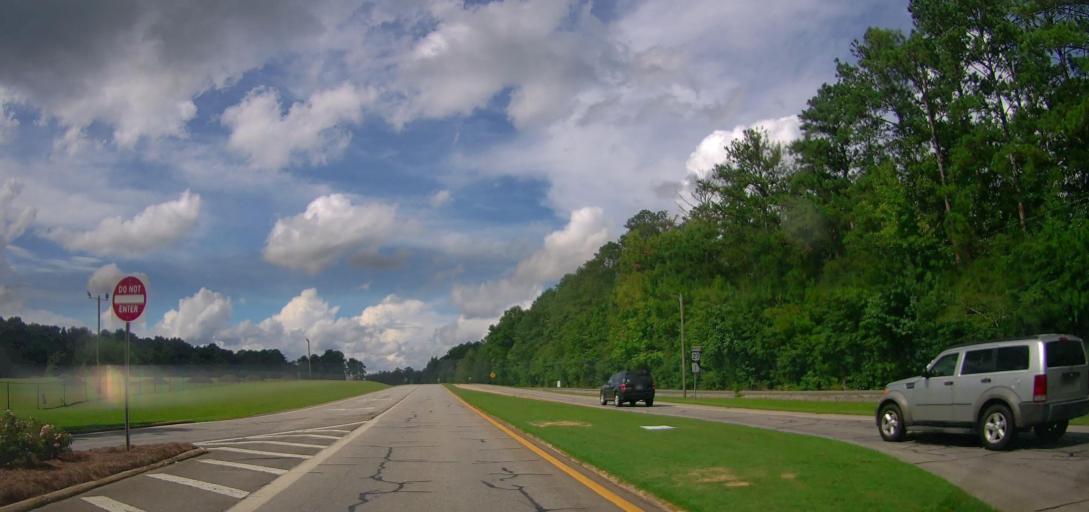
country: US
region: Georgia
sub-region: Harris County
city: Pine Mountain
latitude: 32.8479
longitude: -84.8448
